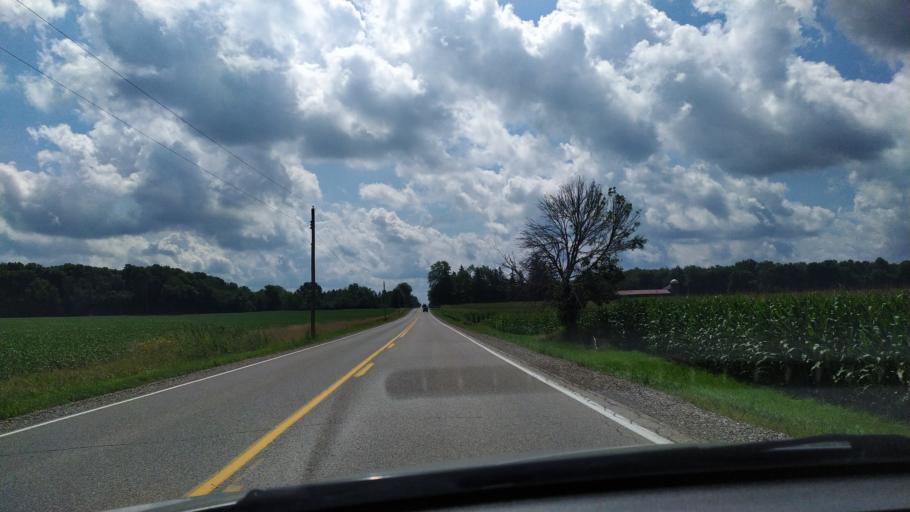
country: CA
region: Ontario
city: London
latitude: 43.0525
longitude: -81.3284
